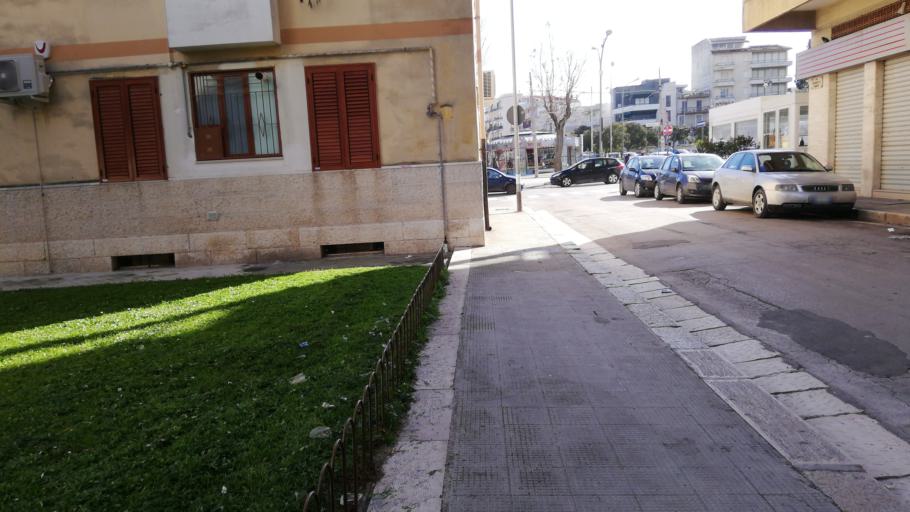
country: IT
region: Apulia
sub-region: Provincia di Barletta - Andria - Trani
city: Andria
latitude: 41.2318
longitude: 16.3041
